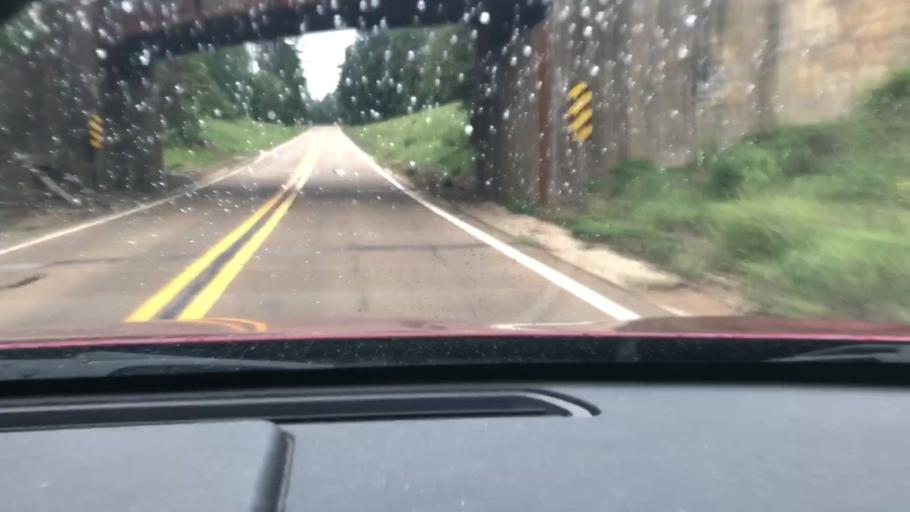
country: US
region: Arkansas
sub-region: Lafayette County
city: Stamps
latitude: 33.3541
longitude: -93.4002
